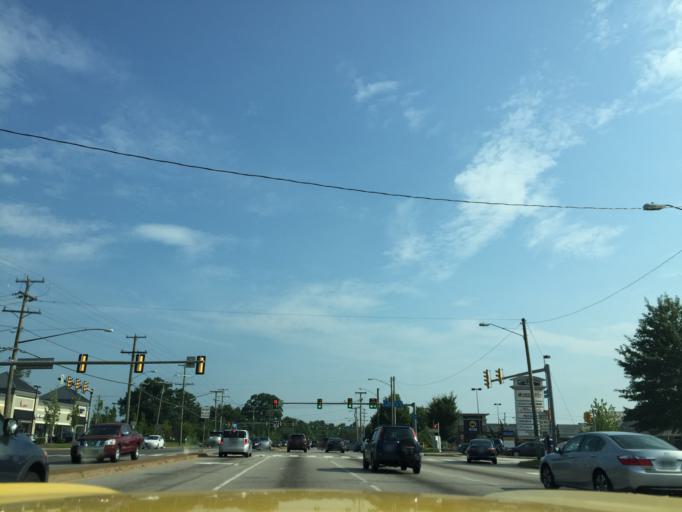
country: US
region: Virginia
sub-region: Fairfax County
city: Hybla Valley
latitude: 38.7500
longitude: -77.0832
